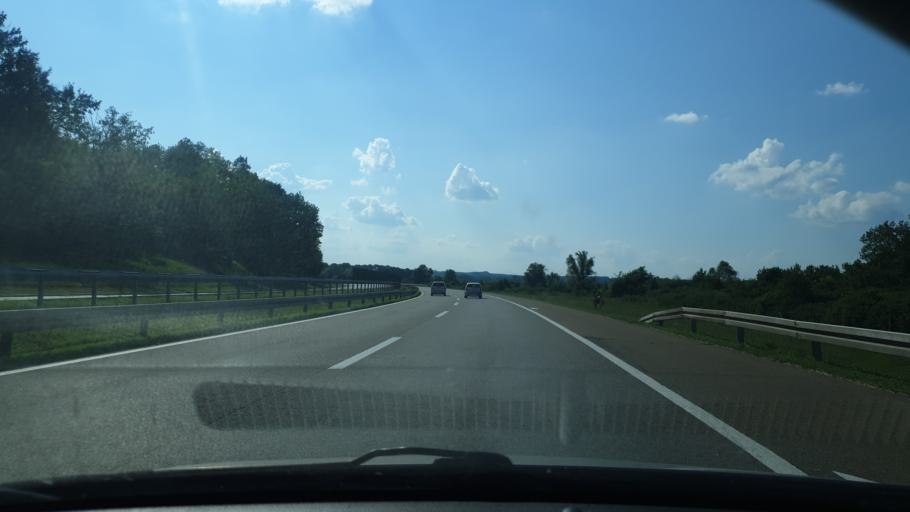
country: RS
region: Central Serbia
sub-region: Podunavski Okrug
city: Smederevo
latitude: 44.5860
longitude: 20.8648
